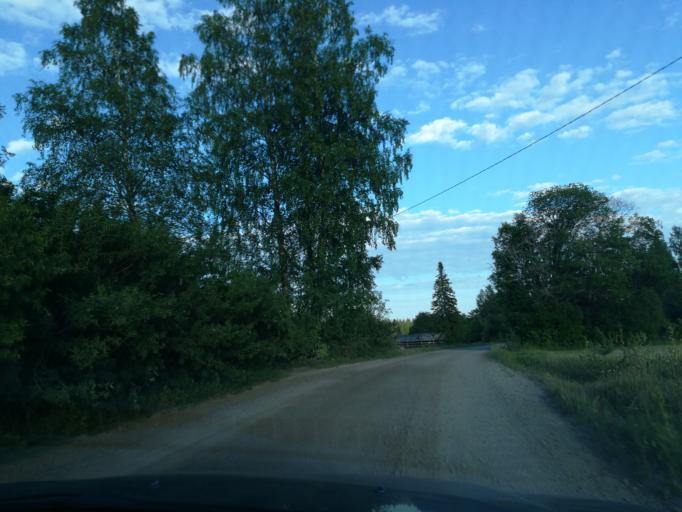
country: FI
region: Southern Savonia
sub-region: Mikkeli
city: Puumala
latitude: 61.5909
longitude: 28.1155
